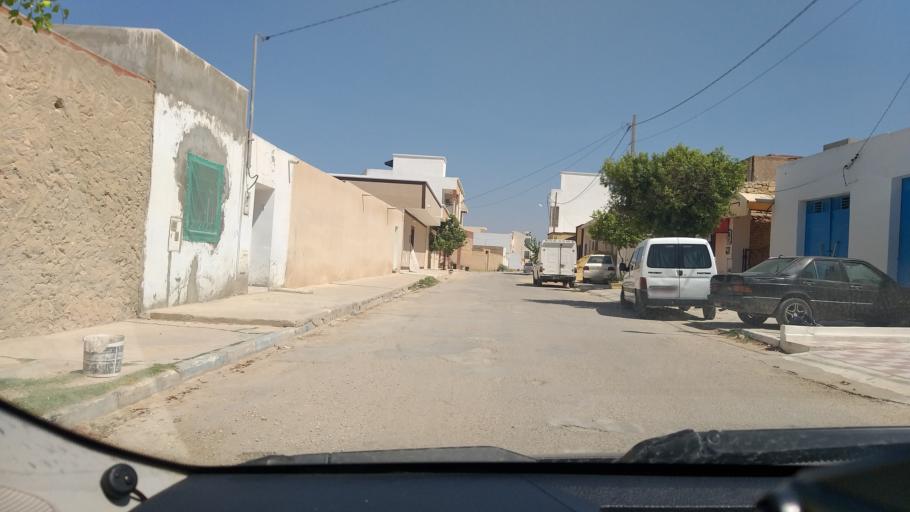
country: TN
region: Al Mahdiyah
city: El Jem
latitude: 35.2915
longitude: 10.7153
